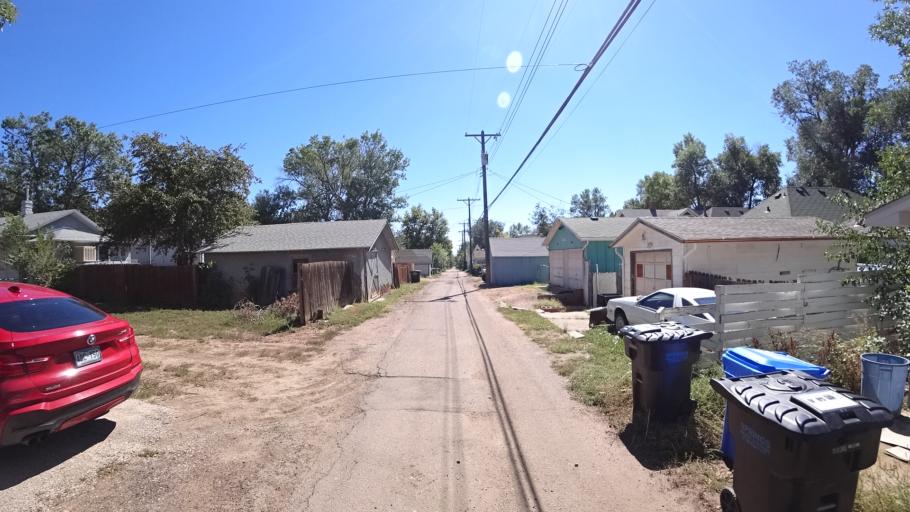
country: US
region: Colorado
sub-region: El Paso County
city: Colorado Springs
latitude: 38.8469
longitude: -104.8576
